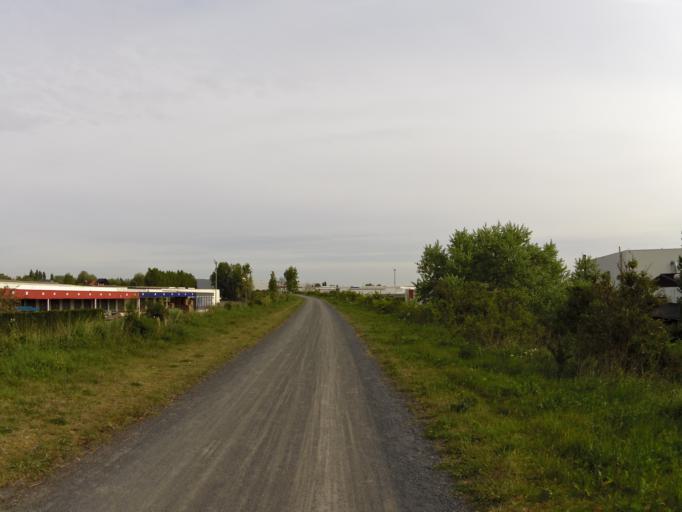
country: BE
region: Flanders
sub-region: Provincie West-Vlaanderen
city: Ostend
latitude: 51.2083
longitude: 2.9579
